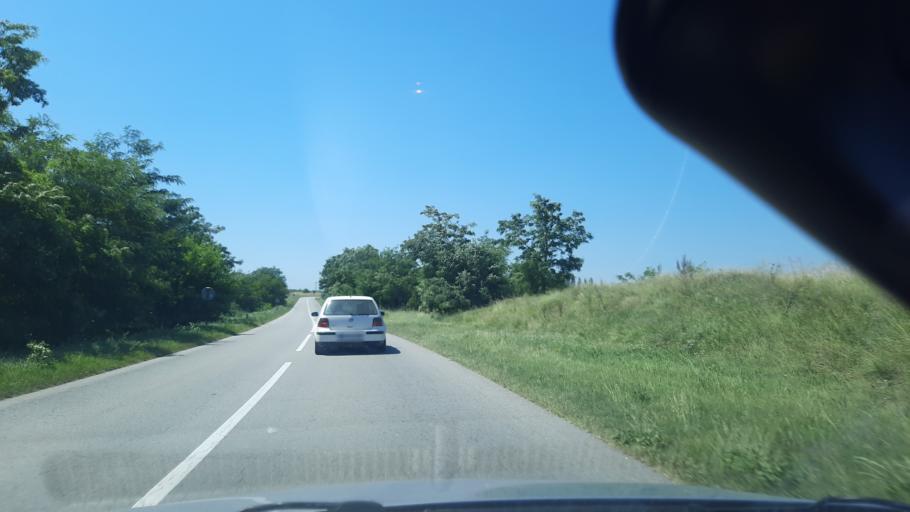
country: RS
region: Central Serbia
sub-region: Branicevski Okrug
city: Pozarevac
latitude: 44.8074
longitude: 21.1709
